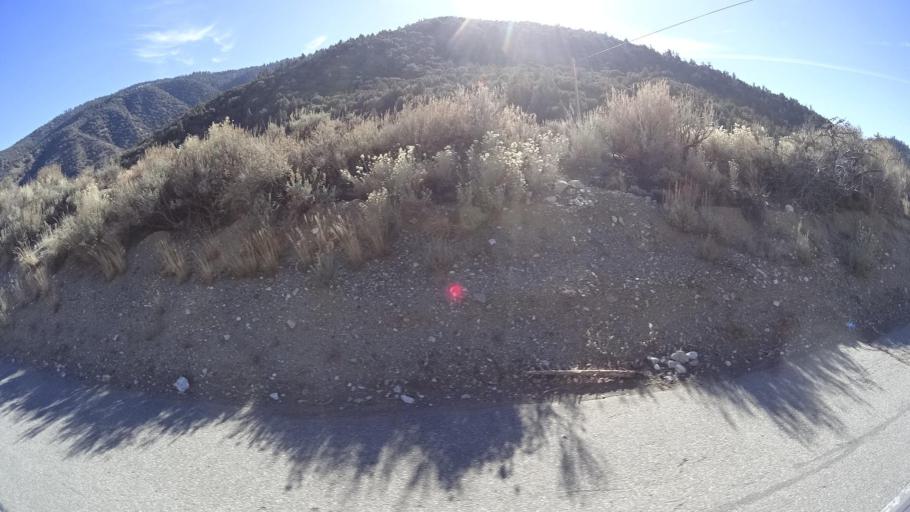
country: US
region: California
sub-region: Kern County
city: Frazier Park
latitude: 34.8202
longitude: -118.9831
